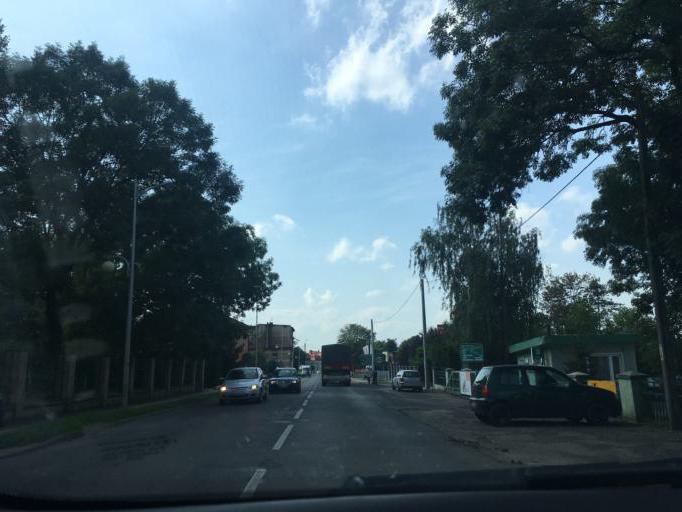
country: PL
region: Opole Voivodeship
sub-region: Powiat glubczycki
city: Glubczyce
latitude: 50.1951
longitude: 17.8381
